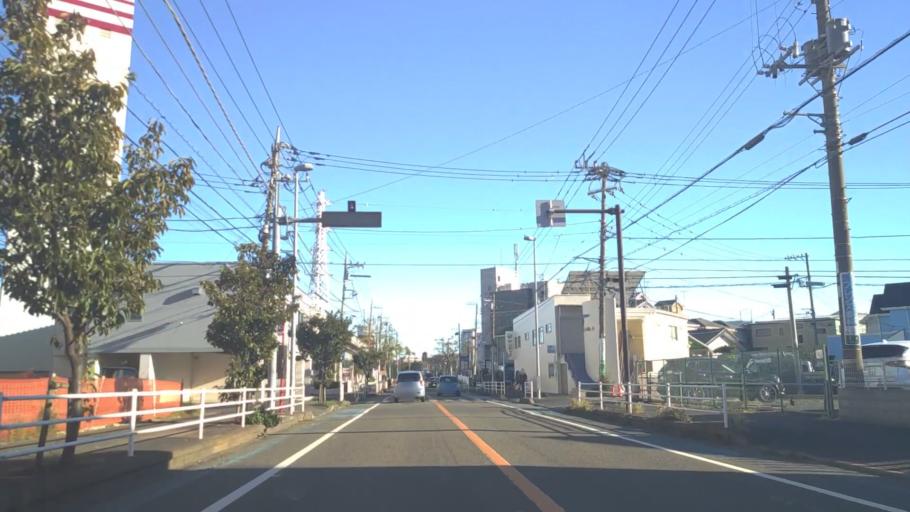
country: JP
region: Kanagawa
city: Chigasaki
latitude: 35.3399
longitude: 139.4010
